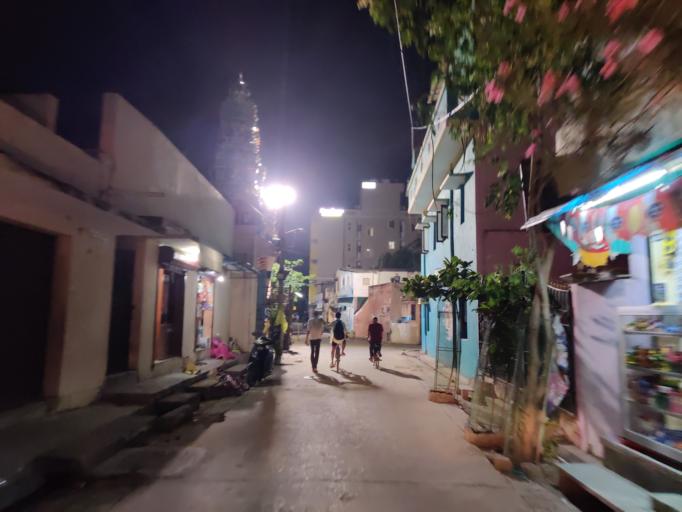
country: IN
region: Pondicherry
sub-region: Puducherry
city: Puducherry
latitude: 11.9456
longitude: 79.8361
